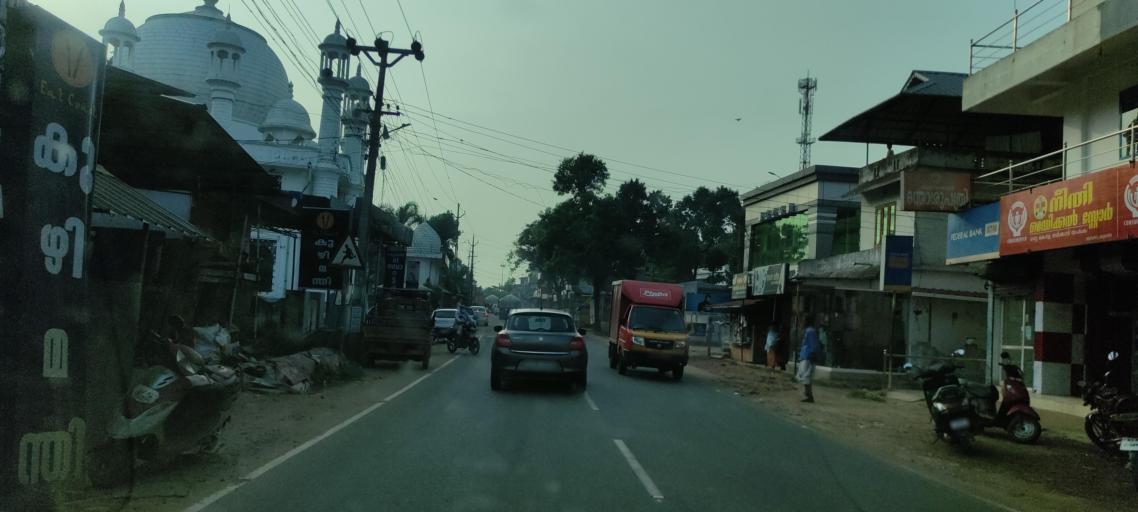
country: IN
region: Kerala
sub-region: Pattanamtitta
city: Adur
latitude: 9.1665
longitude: 76.6666
